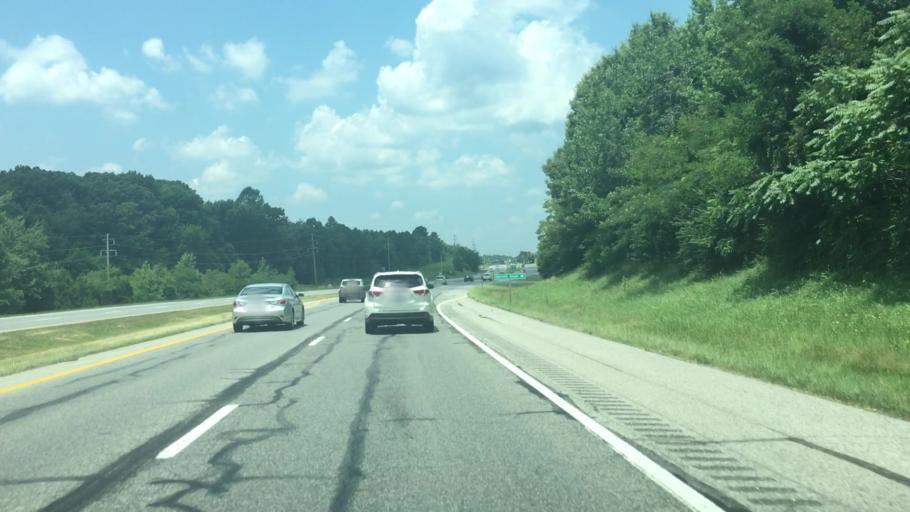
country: US
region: Maryland
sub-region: Saint Mary's County
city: California
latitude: 38.3419
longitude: -76.5677
